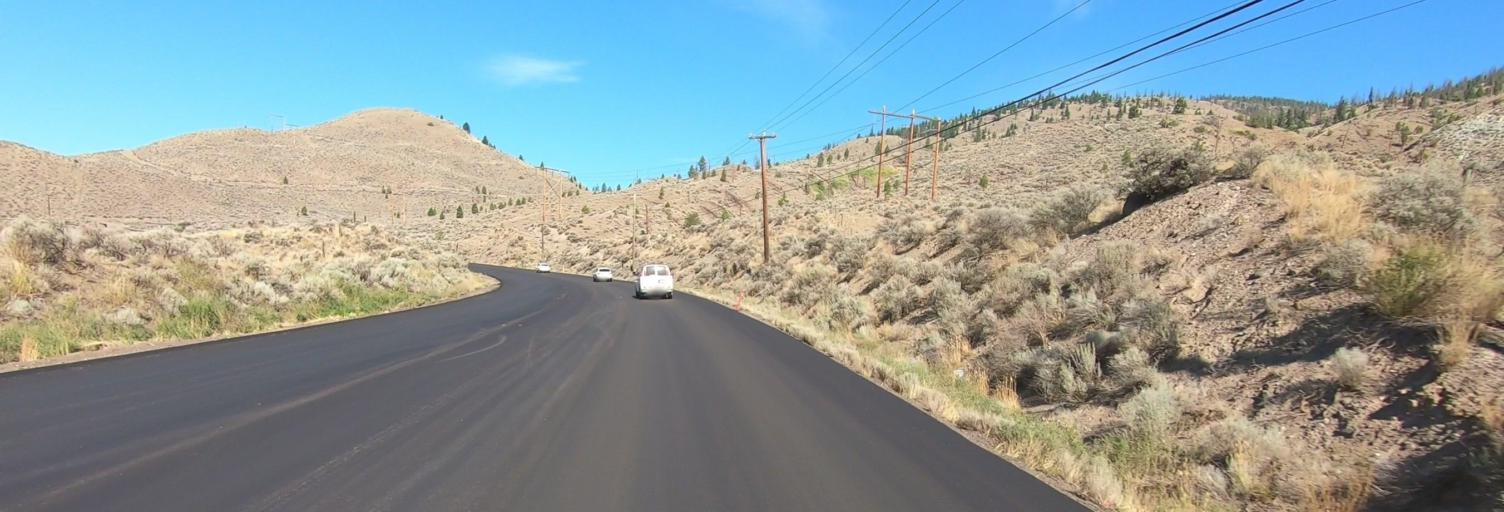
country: CA
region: British Columbia
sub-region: Thompson-Nicola Regional District
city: Ashcroft
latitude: 50.7979
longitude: -121.1016
